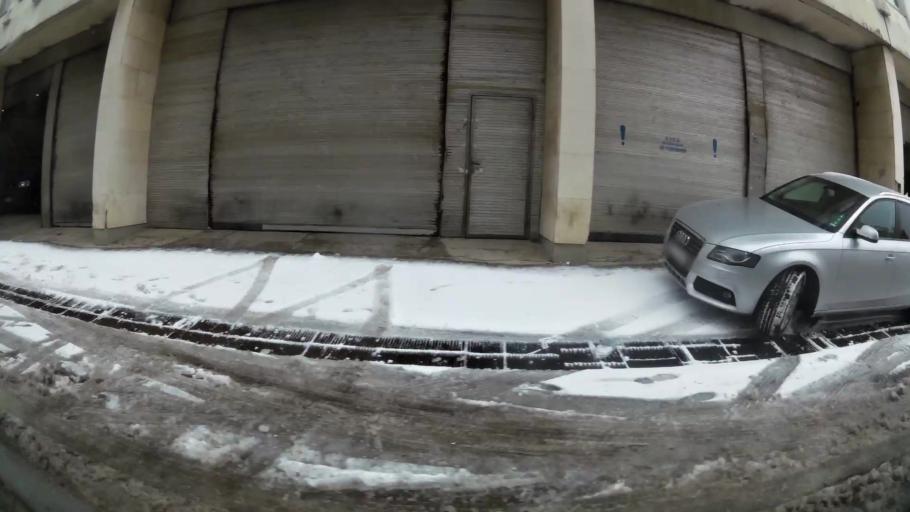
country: BG
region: Sofia-Capital
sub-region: Stolichna Obshtina
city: Sofia
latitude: 42.6972
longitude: 23.3122
